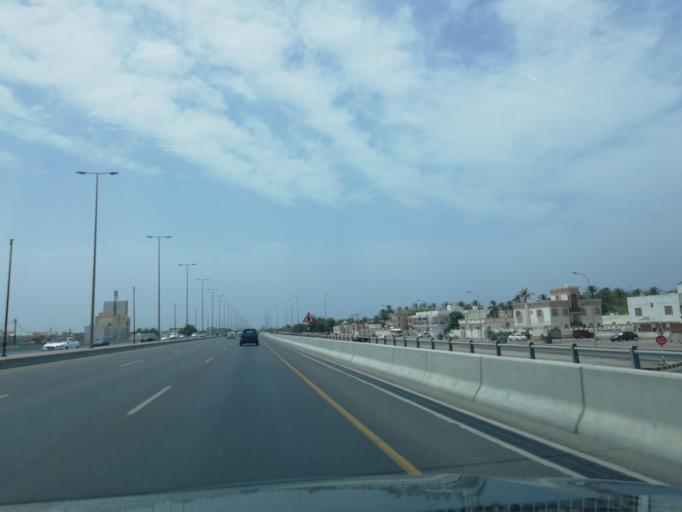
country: OM
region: Muhafazat Masqat
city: As Sib al Jadidah
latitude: 23.6691
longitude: 58.1515
